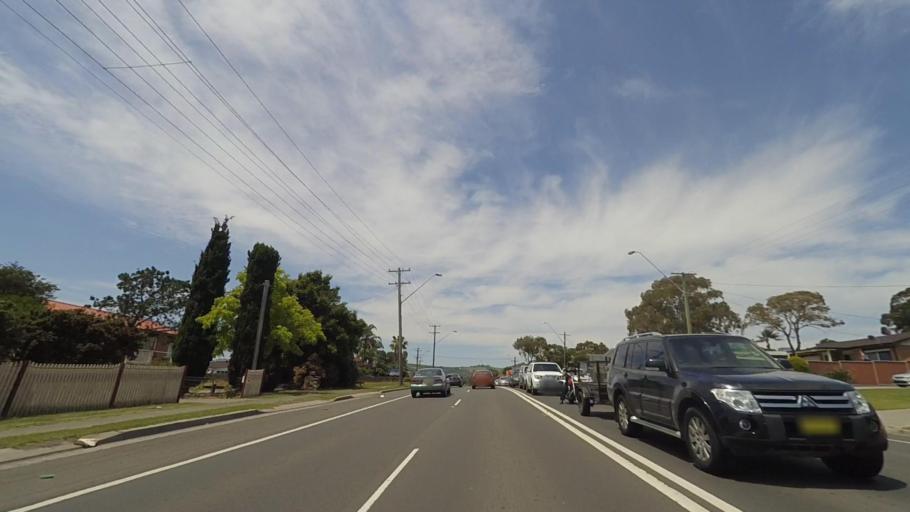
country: AU
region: New South Wales
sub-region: Shellharbour
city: Albion Park Rail
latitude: -34.5656
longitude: 150.8001
